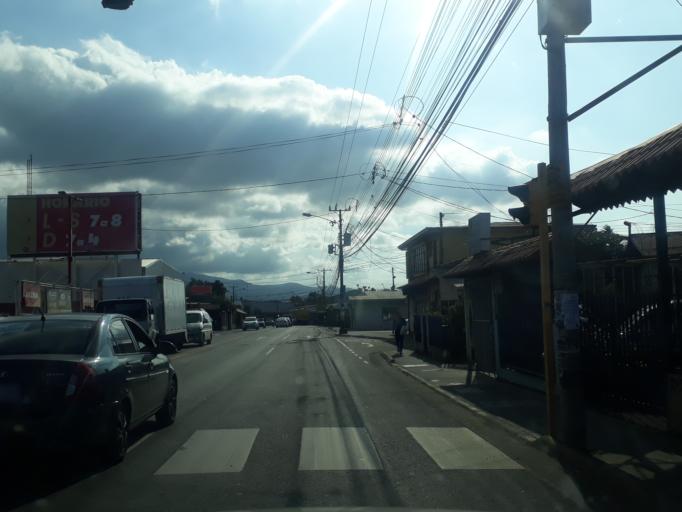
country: CR
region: San Jose
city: San Vicente
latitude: 9.9648
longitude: -84.0399
